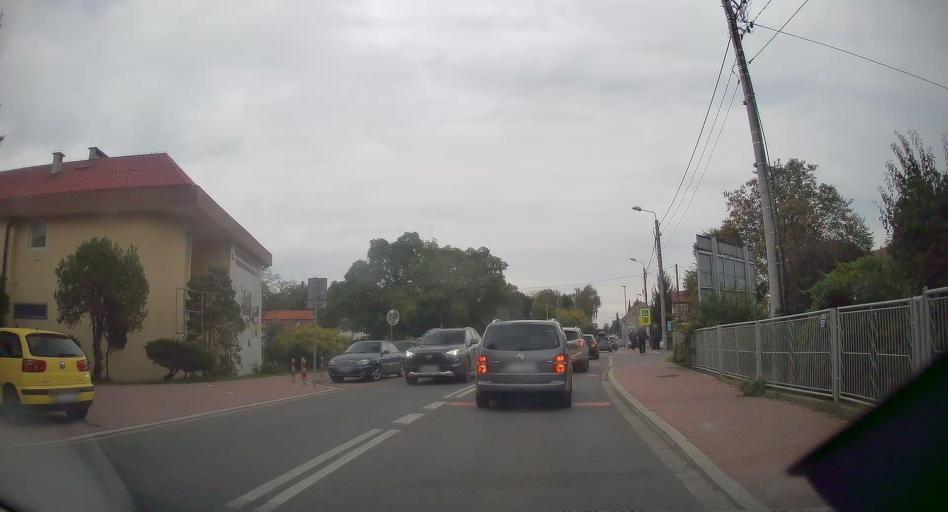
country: PL
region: Lesser Poland Voivodeship
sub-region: Powiat wielicki
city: Niepolomice
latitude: 50.0357
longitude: 20.2153
